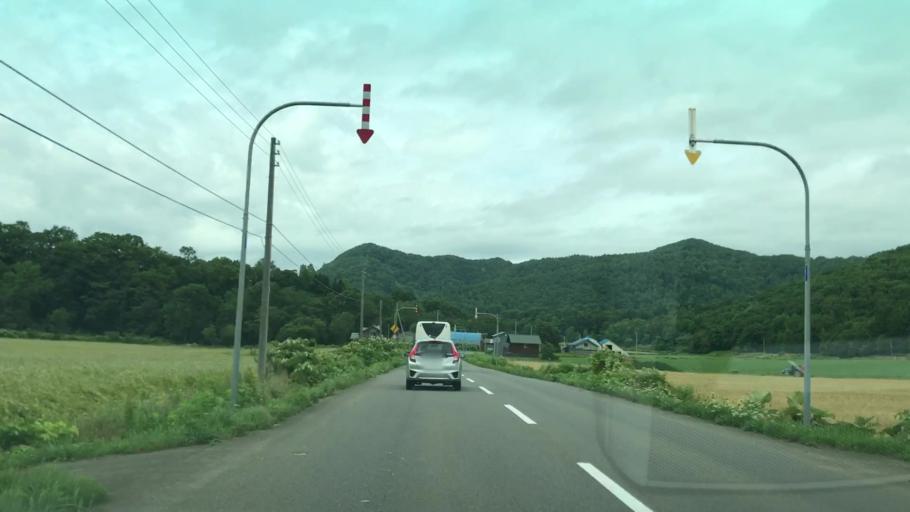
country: JP
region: Hokkaido
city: Niseko Town
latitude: 42.9474
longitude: 140.8356
